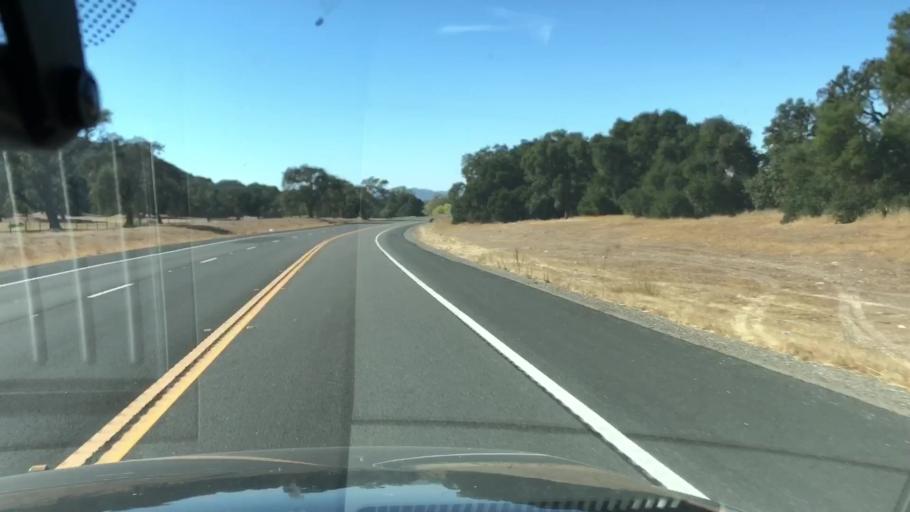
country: US
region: California
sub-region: Santa Barbara County
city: Santa Ynez
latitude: 34.5878
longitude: -120.0238
